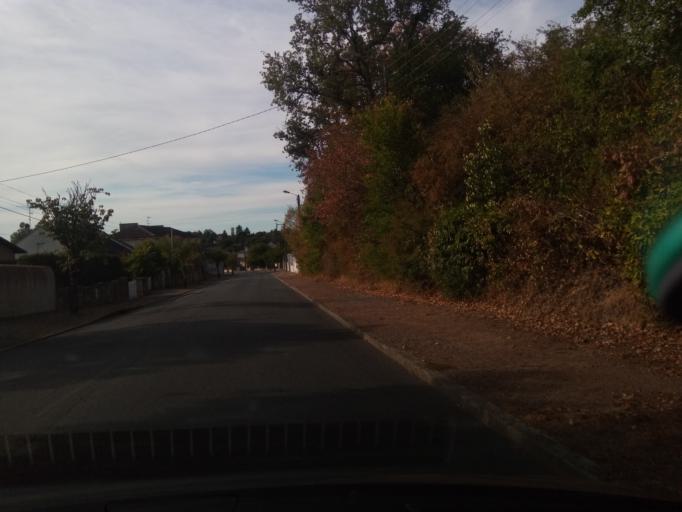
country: FR
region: Poitou-Charentes
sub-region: Departement de la Vienne
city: Montmorillon
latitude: 46.4175
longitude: 0.8804
